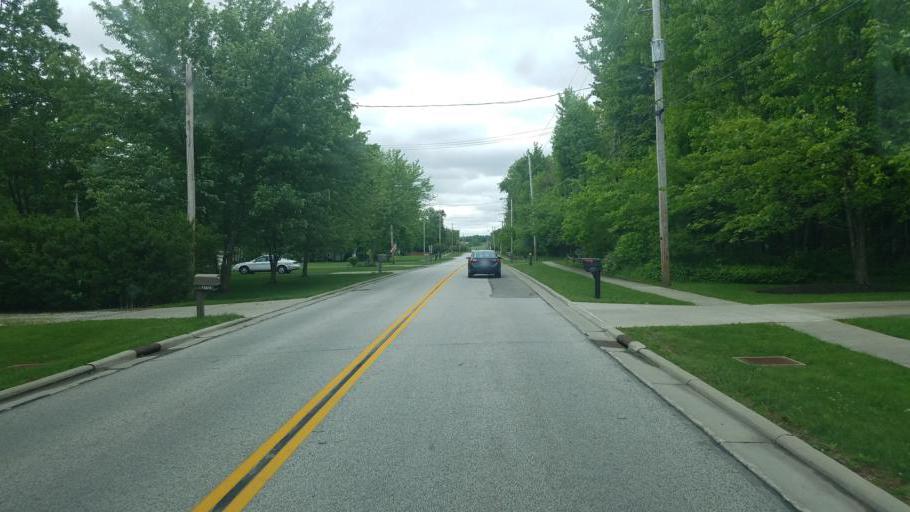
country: US
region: Ohio
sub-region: Summit County
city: Twinsburg
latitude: 41.3329
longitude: -81.4339
